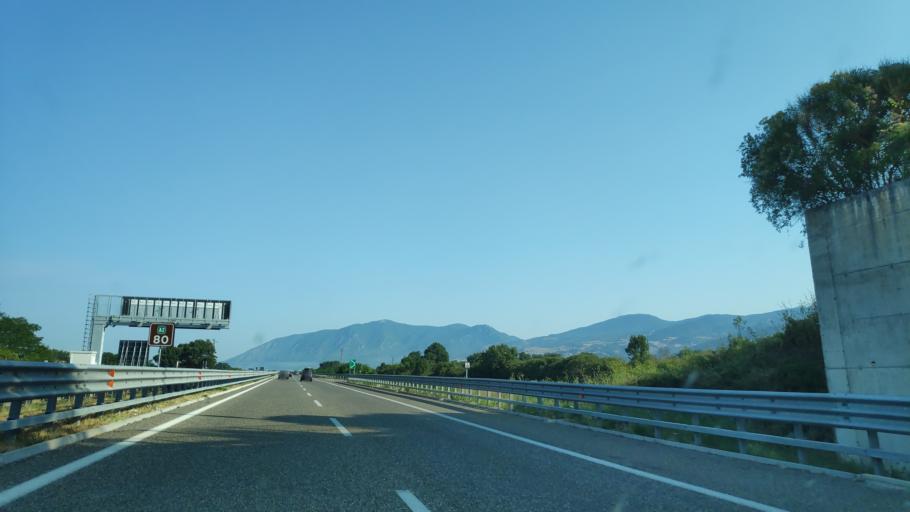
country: IT
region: Campania
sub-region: Provincia di Salerno
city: Padula
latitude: 40.3146
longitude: 15.6411
